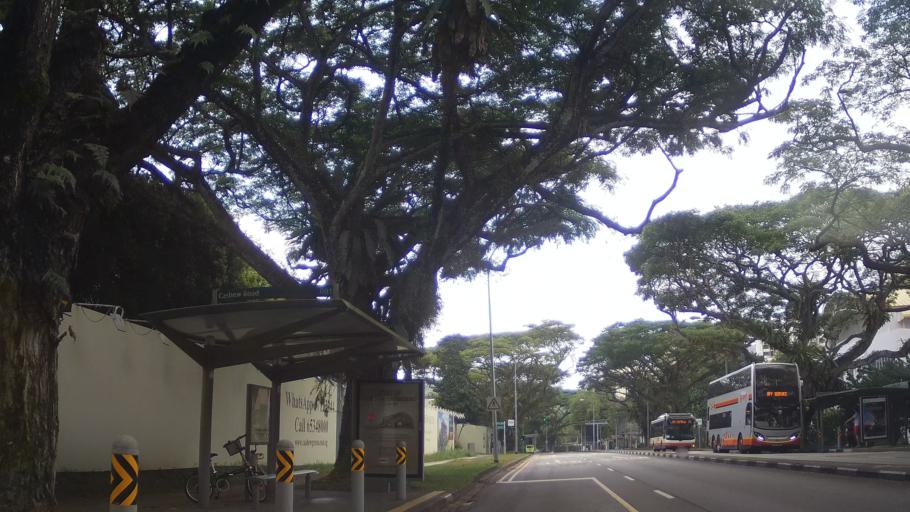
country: MY
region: Johor
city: Johor Bahru
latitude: 1.3733
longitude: 103.7705
